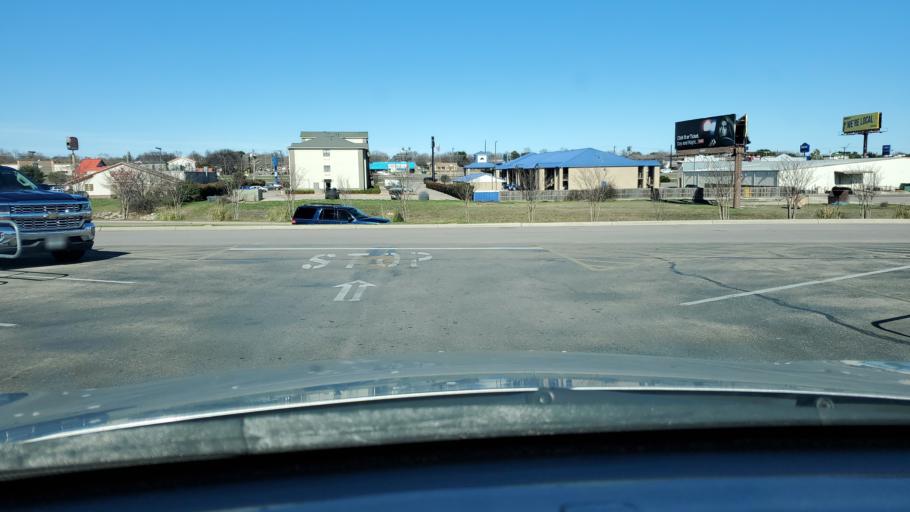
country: US
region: Texas
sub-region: Bell County
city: Killeen
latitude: 31.0907
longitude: -97.7280
